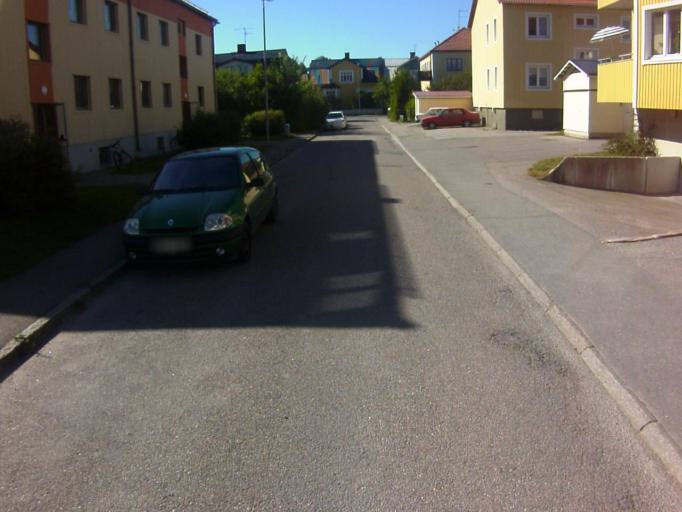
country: SE
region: Soedermanland
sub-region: Eskilstuna Kommun
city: Eskilstuna
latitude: 59.3808
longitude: 16.5156
